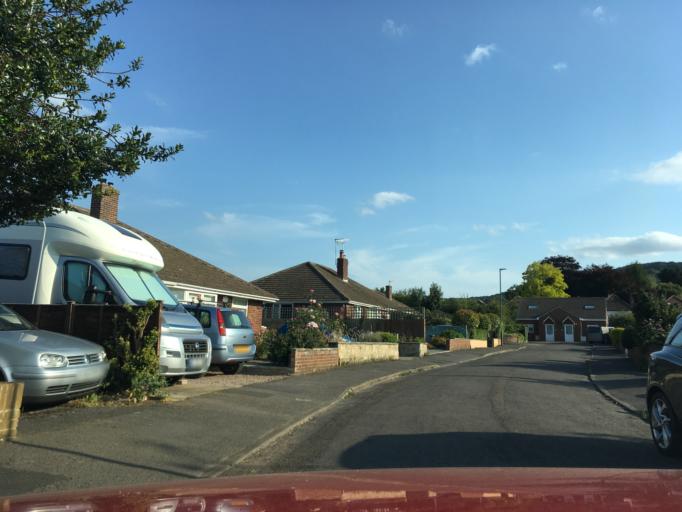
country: GB
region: England
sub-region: Gloucestershire
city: Shurdington
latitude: 51.8445
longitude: -2.1515
